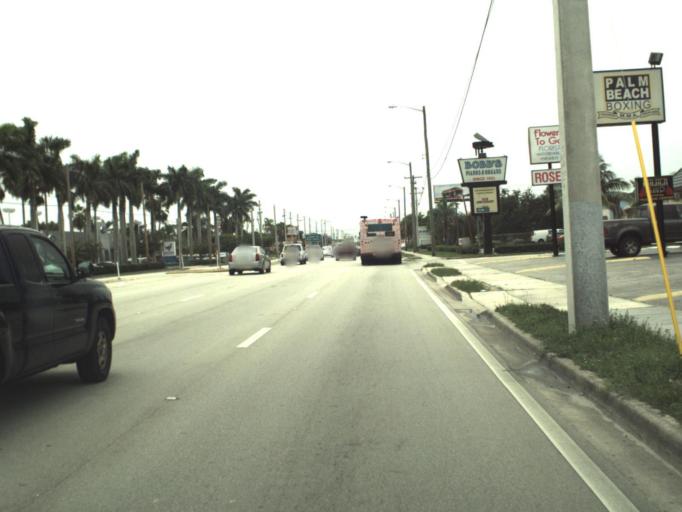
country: US
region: Florida
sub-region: Palm Beach County
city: Haverhill
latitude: 26.7014
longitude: -80.1114
